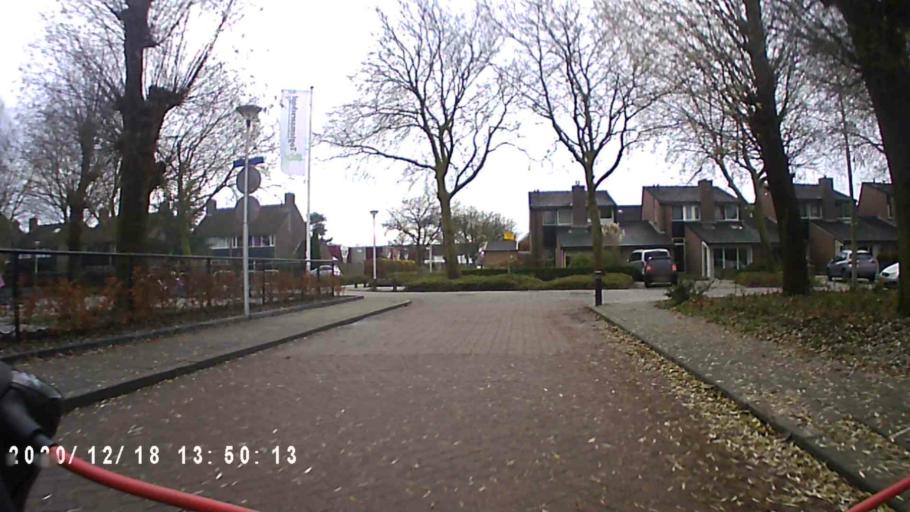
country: NL
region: Groningen
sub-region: Gemeente Bedum
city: Bedum
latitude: 53.3006
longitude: 6.6061
